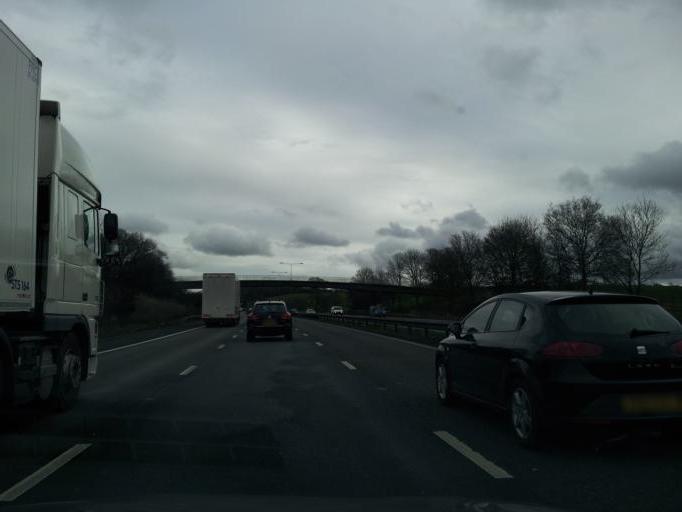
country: GB
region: England
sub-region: Staffordshire
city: Audley
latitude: 52.9982
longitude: -2.3181
